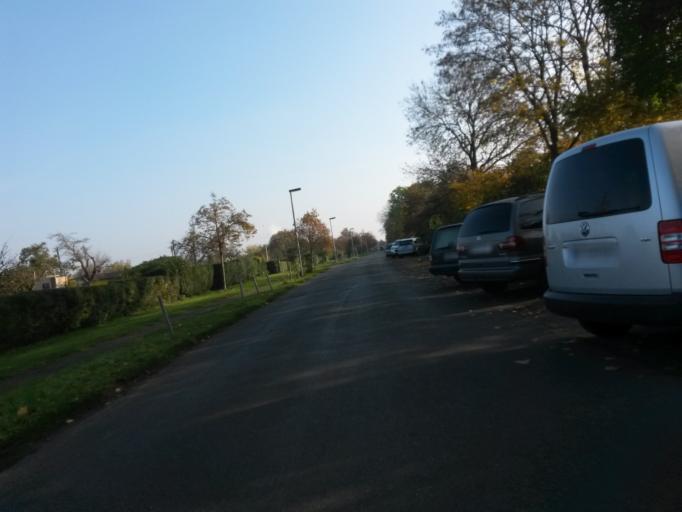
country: DE
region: Bremen
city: Bremen
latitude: 53.0634
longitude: 8.8228
